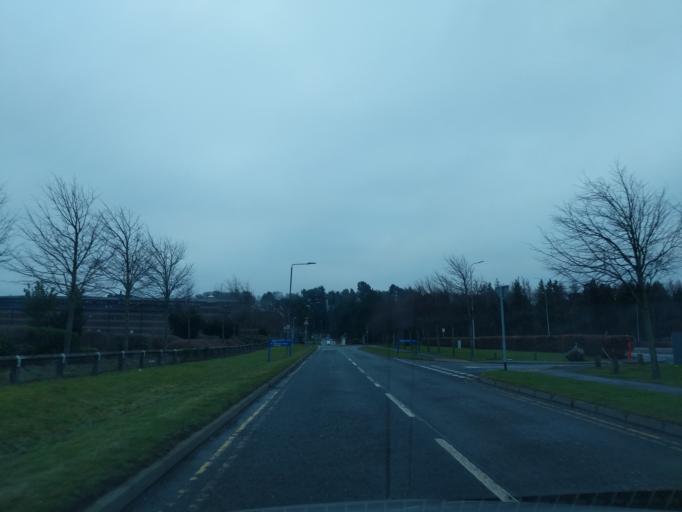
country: GB
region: Scotland
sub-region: Edinburgh
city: Currie
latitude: 55.9122
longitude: -3.3274
